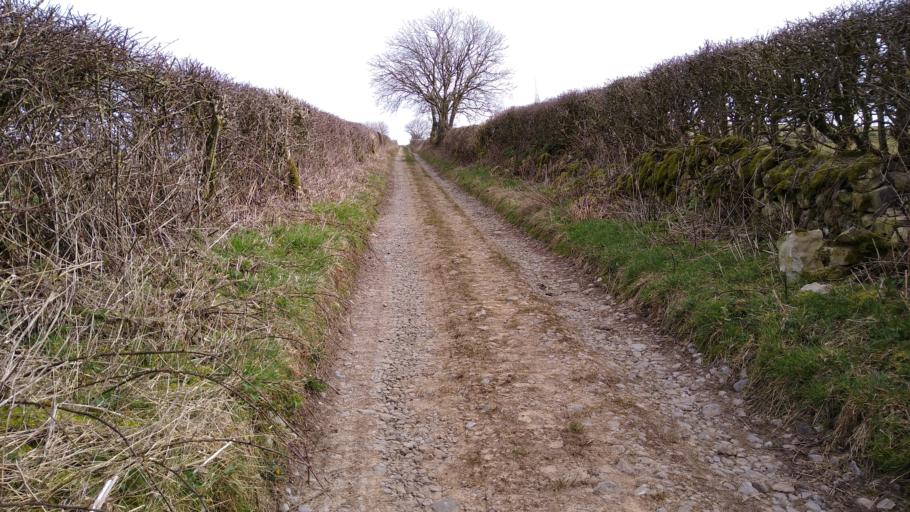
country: GB
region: England
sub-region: Cumbria
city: Cockermouth
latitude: 54.7082
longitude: -3.3702
